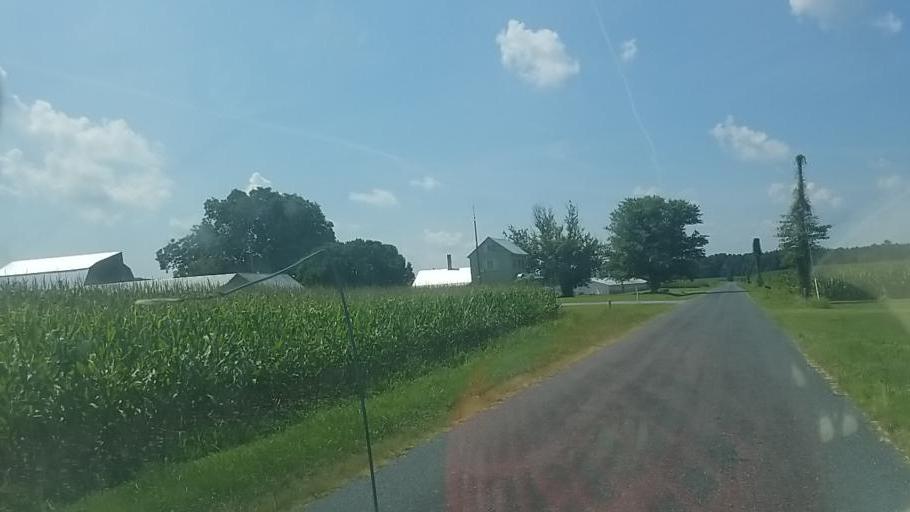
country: US
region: Maryland
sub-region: Worcester County
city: Berlin
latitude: 38.2957
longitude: -75.2928
